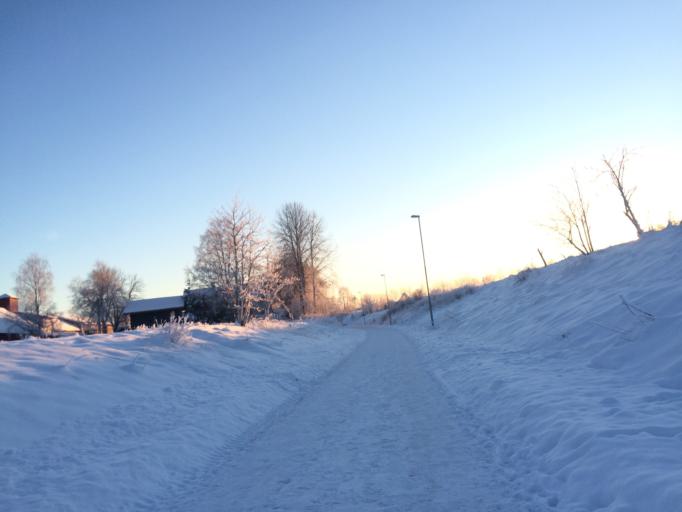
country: NO
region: Akershus
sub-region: Ski
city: Ski
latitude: 59.7036
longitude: 10.8327
